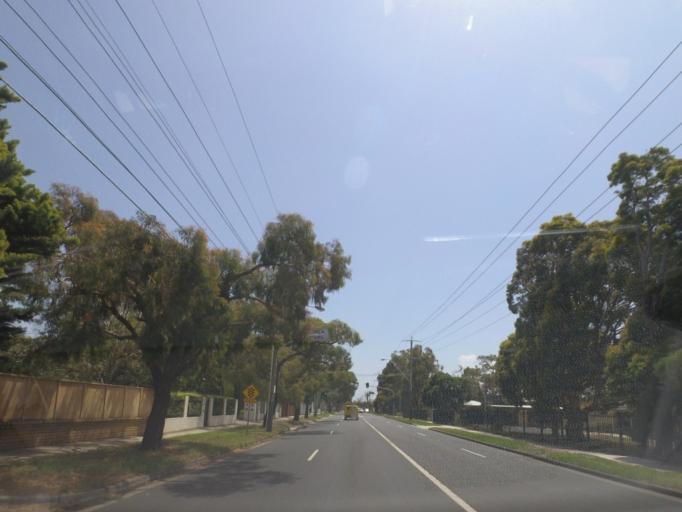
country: AU
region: Victoria
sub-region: Bayside
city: Hampton East
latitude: -37.9519
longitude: 145.0210
